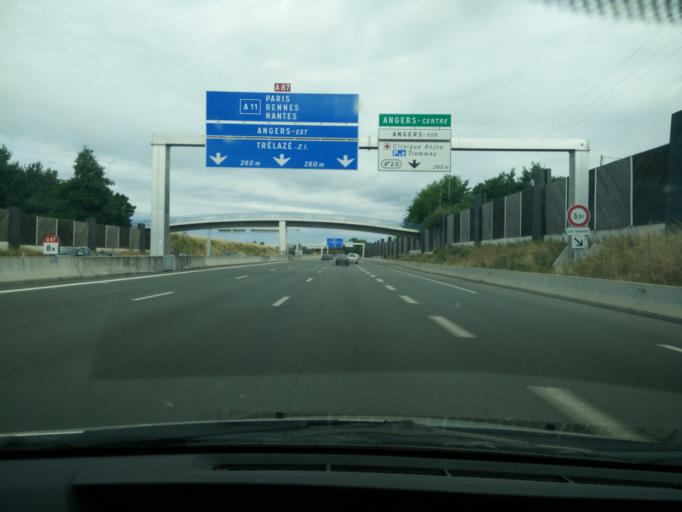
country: FR
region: Pays de la Loire
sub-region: Departement de Maine-et-Loire
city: Les Ponts-de-Ce
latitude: 47.4388
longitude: -0.5105
